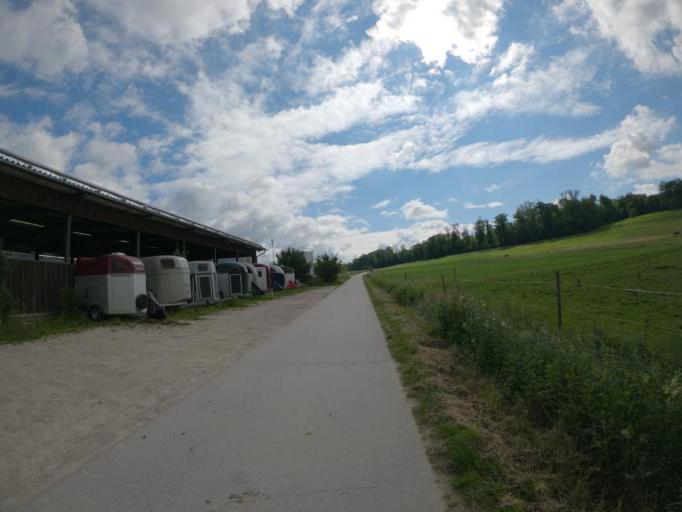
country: DE
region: Baden-Wuerttemberg
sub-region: Regierungsbezirk Stuttgart
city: Schlierbach
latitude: 48.6911
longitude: 9.5157
